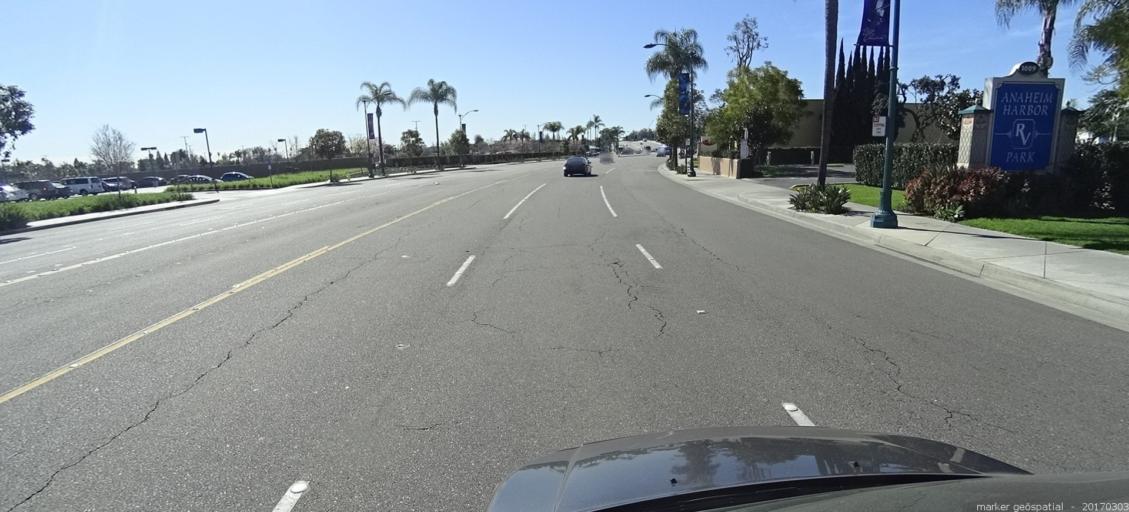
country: US
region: California
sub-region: Orange County
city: Anaheim
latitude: 33.8203
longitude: -117.9151
